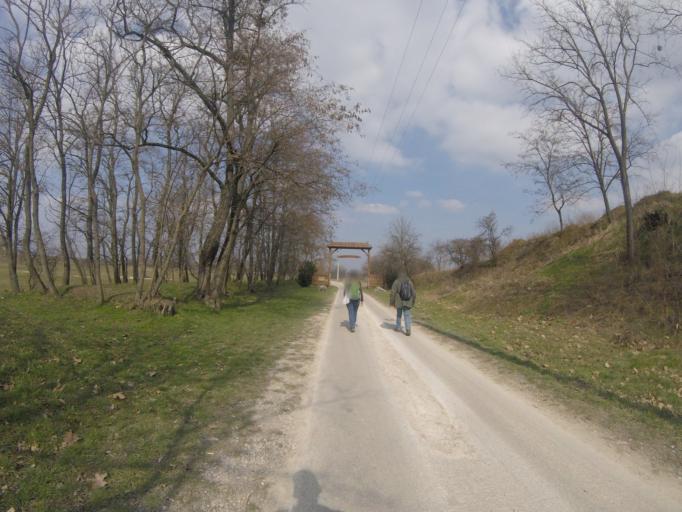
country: HU
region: Komarom-Esztergom
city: Nyergesujfalu
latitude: 47.7452
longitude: 18.5533
